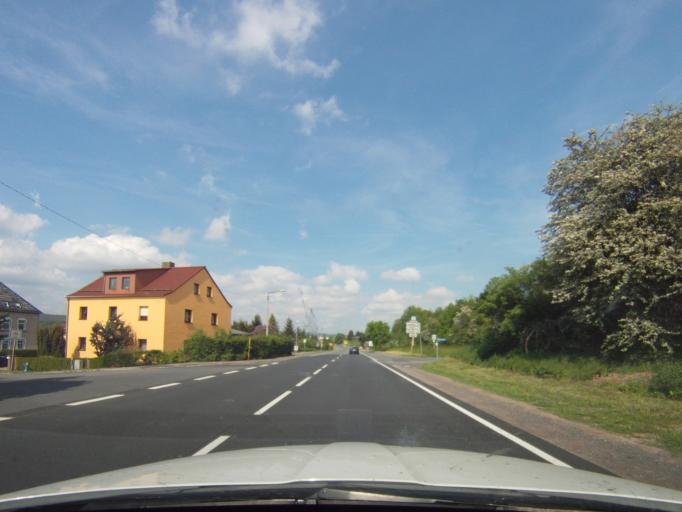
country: DE
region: Thuringia
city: Oppurg
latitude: 50.7081
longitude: 11.6534
